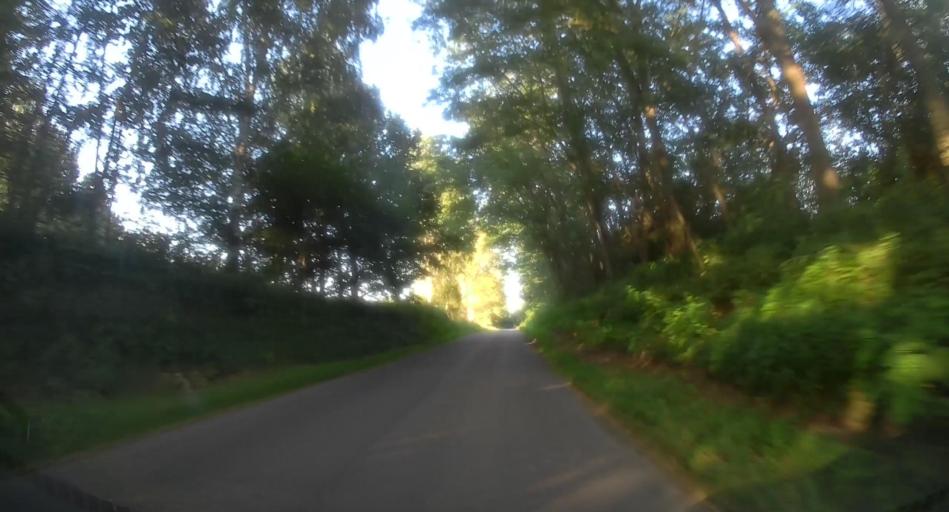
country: PL
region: Lodz Voivodeship
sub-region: Powiat skierniewicki
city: Kaweczyn Nowy
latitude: 51.9025
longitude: 20.3103
